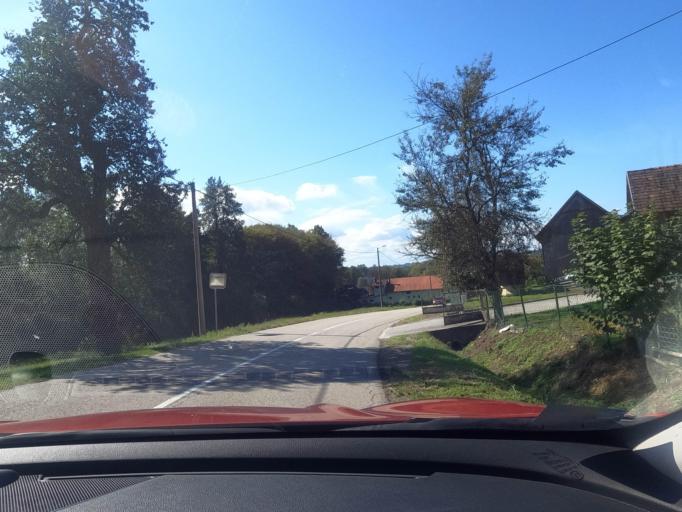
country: BA
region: Federation of Bosnia and Herzegovina
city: Vrnograc
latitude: 45.2595
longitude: 15.9497
